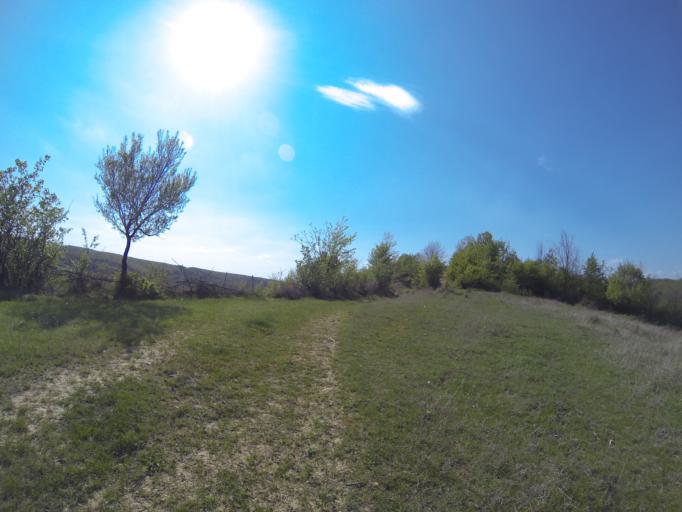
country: RO
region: Gorj
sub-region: Comuna Crusetu
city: Crusetu
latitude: 44.6206
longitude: 23.6542
